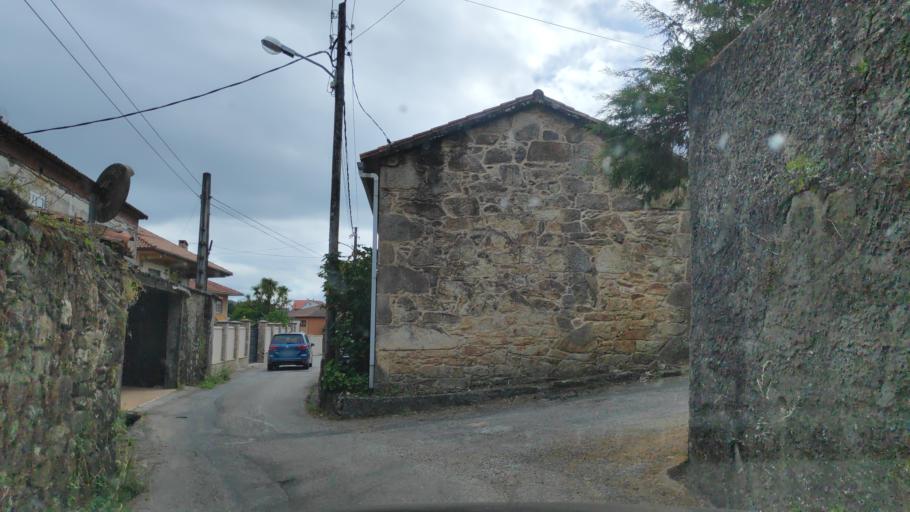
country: ES
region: Galicia
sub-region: Provincia da Coruna
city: Rianxo
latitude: 42.6723
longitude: -8.8137
